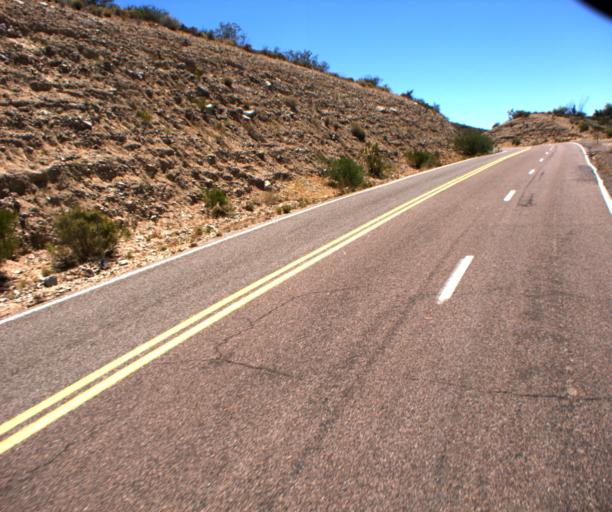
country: US
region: Arizona
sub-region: Yavapai County
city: Bagdad
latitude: 34.4611
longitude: -113.0067
